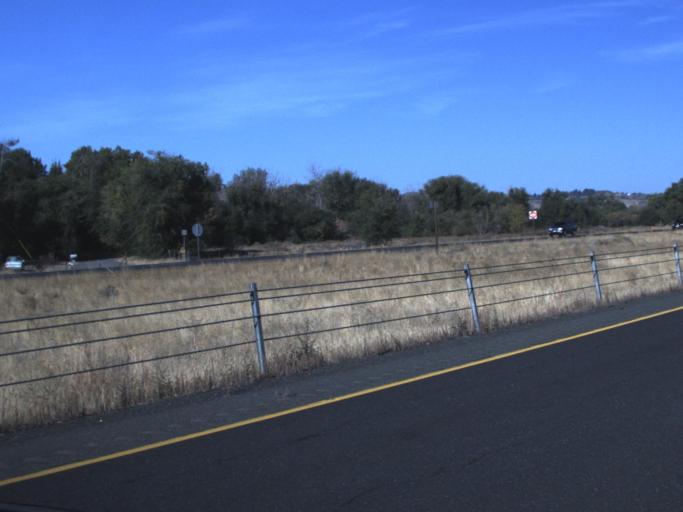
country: US
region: Washington
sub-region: Yakima County
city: Gleed
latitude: 46.6481
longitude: -120.6050
